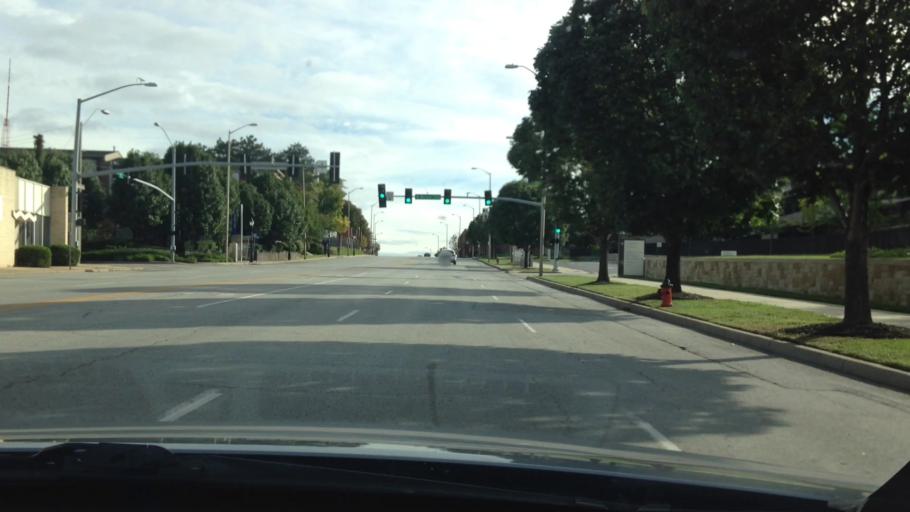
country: US
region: Missouri
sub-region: Jackson County
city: Kansas City
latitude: 39.0754
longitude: -94.5851
